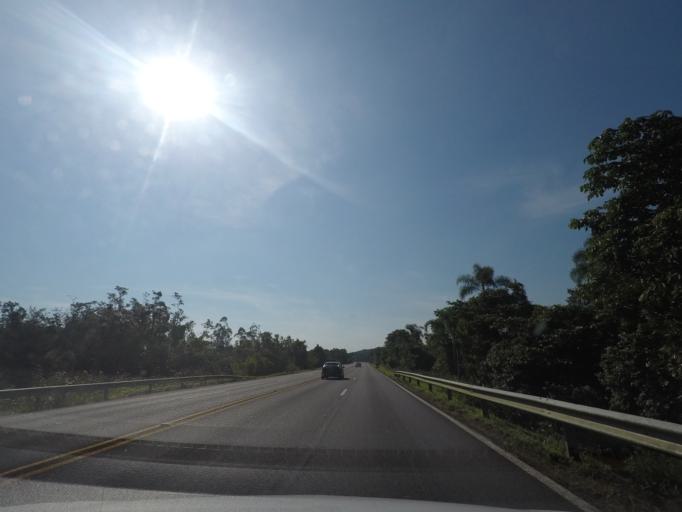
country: BR
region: Parana
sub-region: Paranagua
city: Paranagua
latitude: -25.5789
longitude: -48.6125
